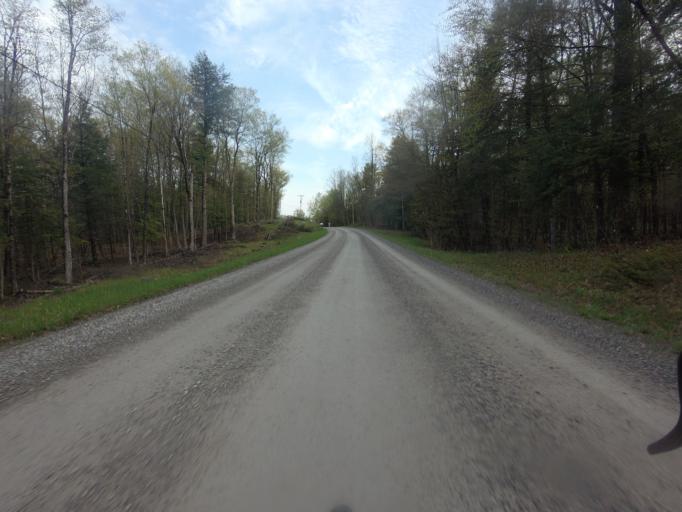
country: CA
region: Ontario
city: Carleton Place
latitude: 45.1960
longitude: -76.3270
